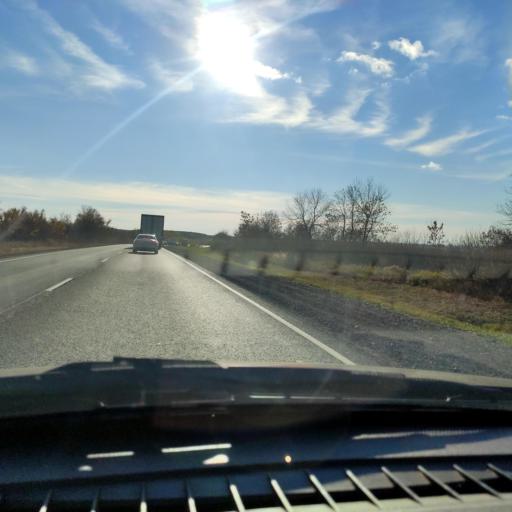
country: RU
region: Samara
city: Zhigulevsk
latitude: 53.3041
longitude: 49.3485
